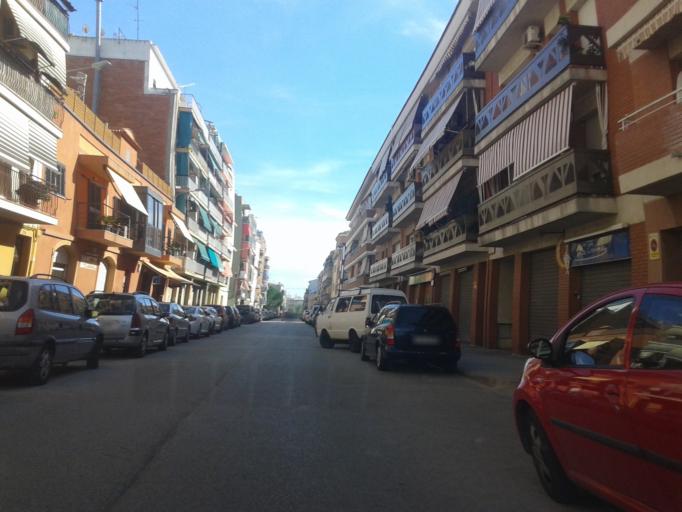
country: ES
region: Catalonia
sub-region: Provincia de Barcelona
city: Vilanova i la Geltru
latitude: 41.2245
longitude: 1.7147
